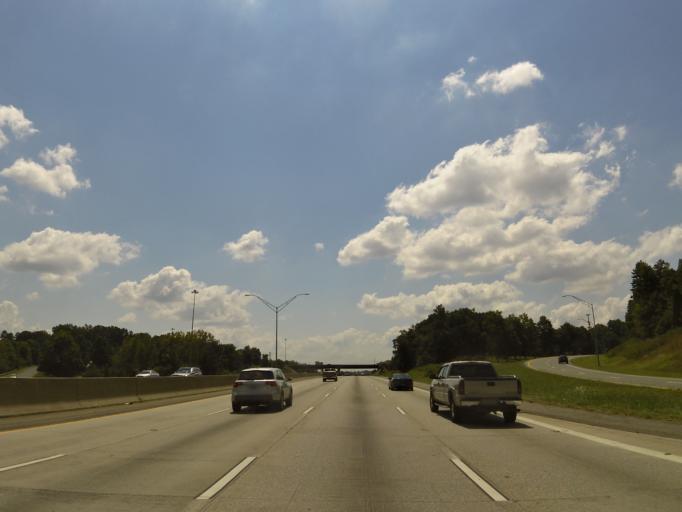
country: US
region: North Carolina
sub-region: Cabarrus County
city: Harrisburg
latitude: 35.3354
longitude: -80.7433
